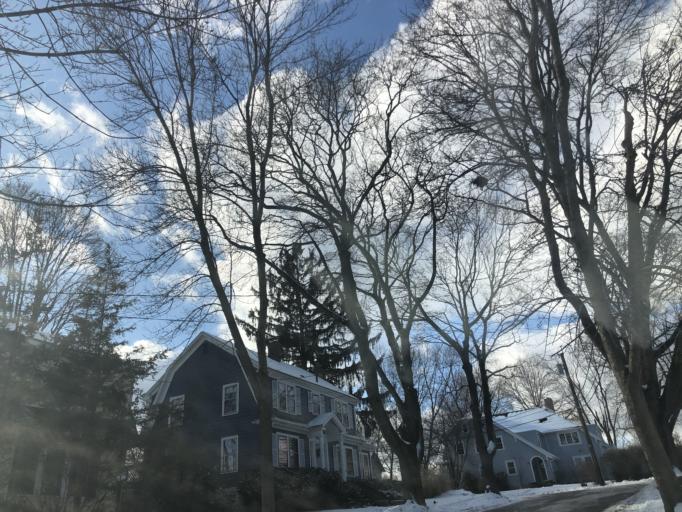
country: US
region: Massachusetts
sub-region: Middlesex County
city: Arlington
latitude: 42.4212
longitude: -71.1458
